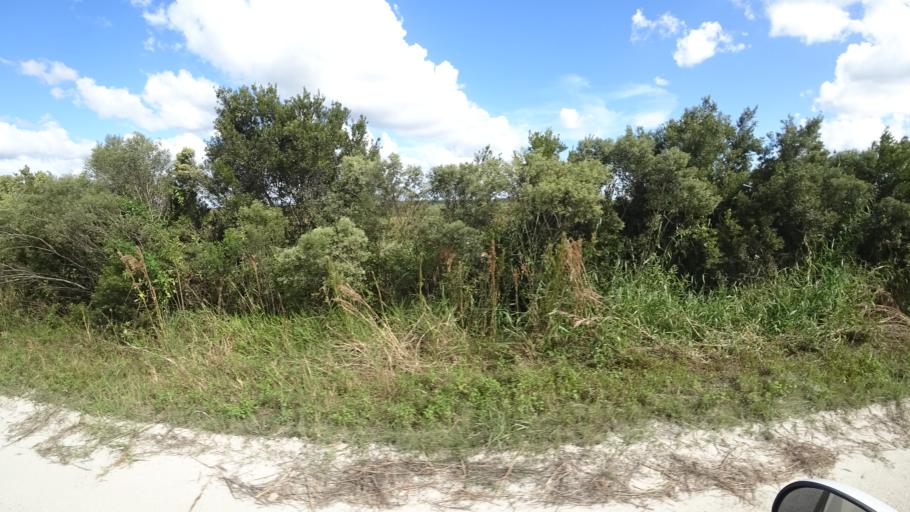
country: US
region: Florida
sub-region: DeSoto County
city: Arcadia
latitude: 27.3285
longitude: -82.1050
